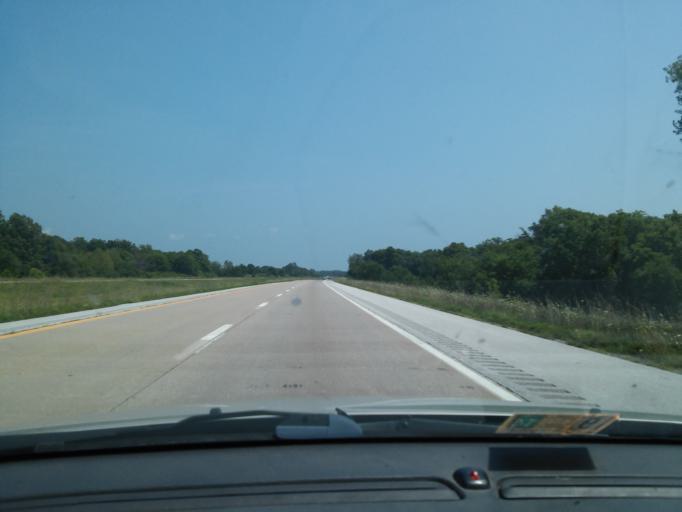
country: US
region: Illinois
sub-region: Scott County
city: Winchester
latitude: 39.6838
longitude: -90.5398
